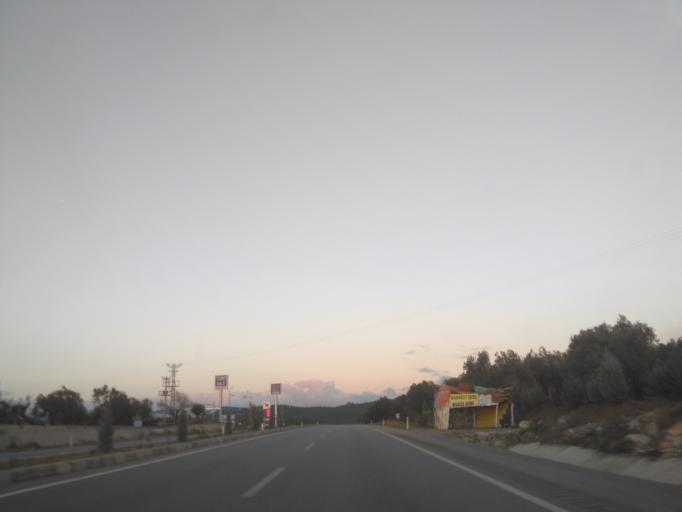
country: TR
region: Balikesir
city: Emrutabat
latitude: 39.4531
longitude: 26.8839
